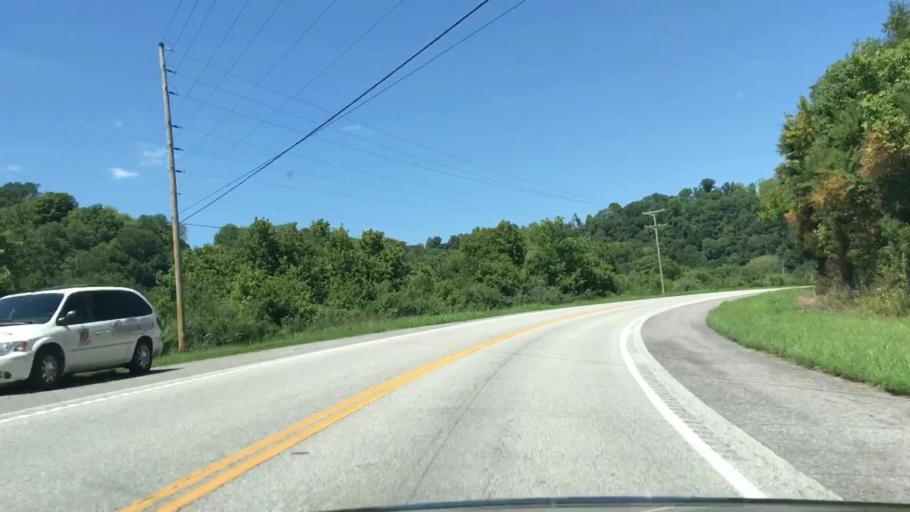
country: US
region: Tennessee
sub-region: Clay County
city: Celina
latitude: 36.4952
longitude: -85.5534
